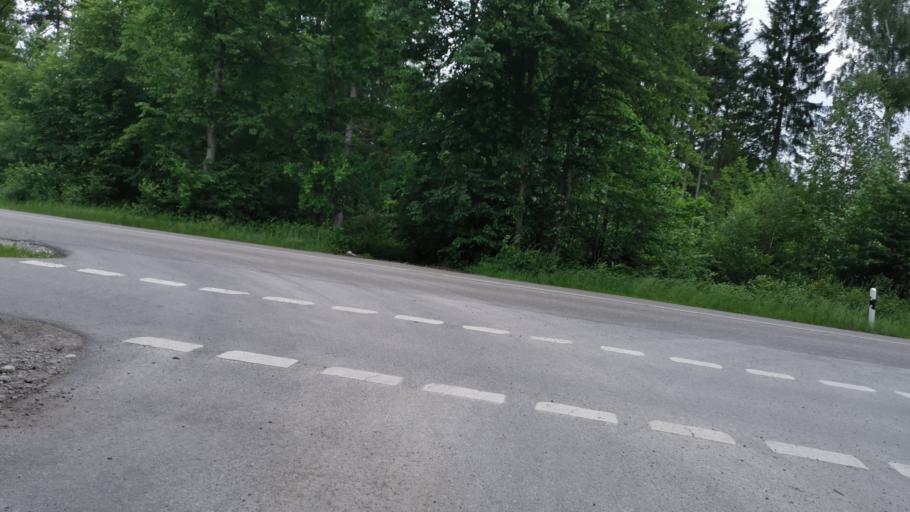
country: DE
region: Bavaria
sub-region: Upper Bavaria
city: Krailling
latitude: 48.0978
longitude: 11.3752
